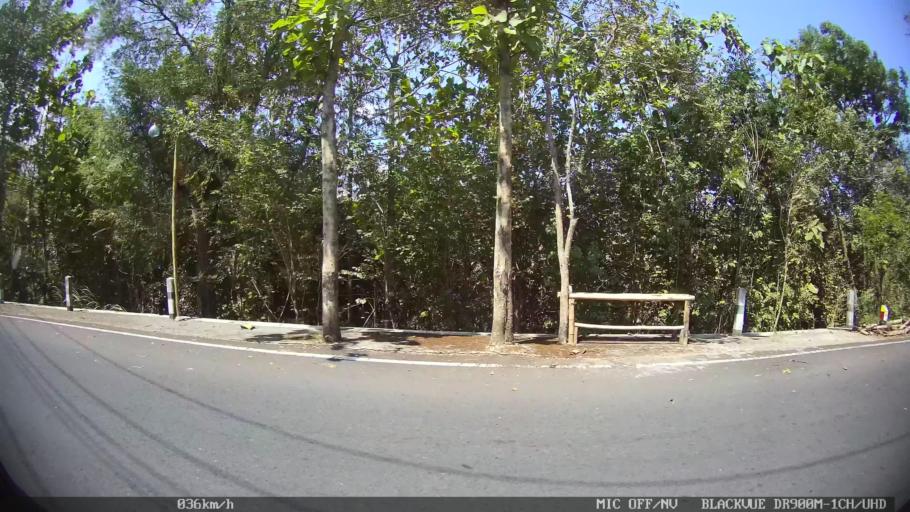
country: ID
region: Daerah Istimewa Yogyakarta
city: Pundong
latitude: -7.9581
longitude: 110.3744
